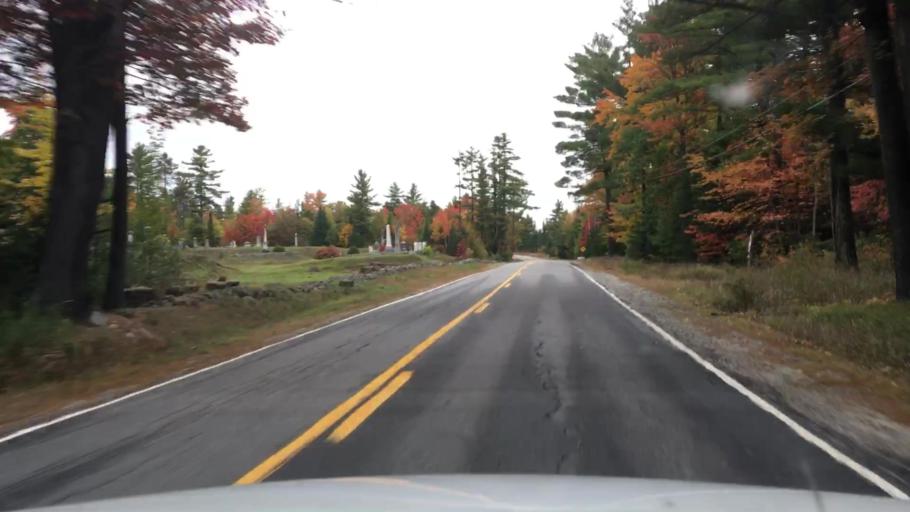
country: US
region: Maine
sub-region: Oxford County
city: Bethel
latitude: 44.3891
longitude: -70.7971
